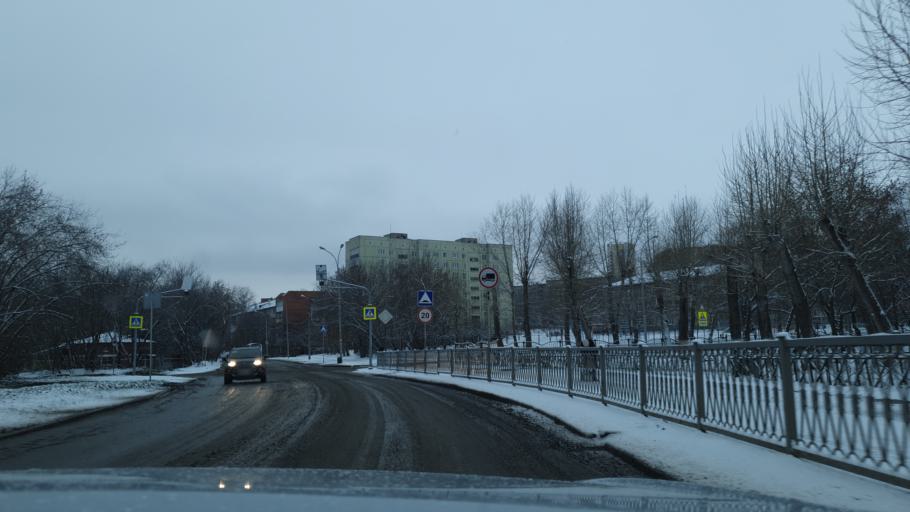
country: RU
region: Sverdlovsk
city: Istok
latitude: 56.7495
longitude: 60.7013
